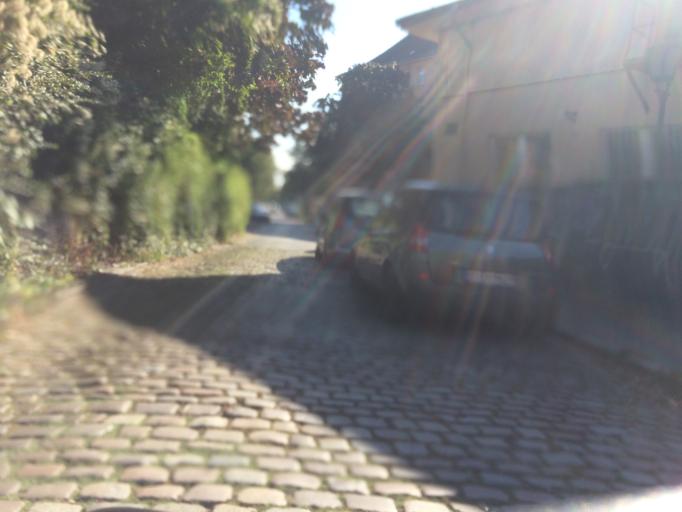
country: DE
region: Berlin
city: Berlin Treptow
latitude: 52.4755
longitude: 13.4302
